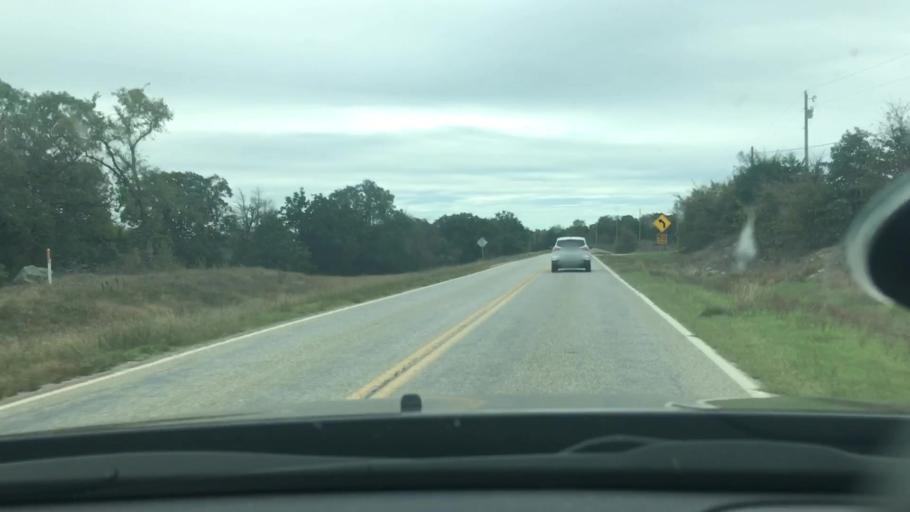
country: US
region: Oklahoma
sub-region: Johnston County
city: Tishomingo
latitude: 34.3242
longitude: -96.4225
